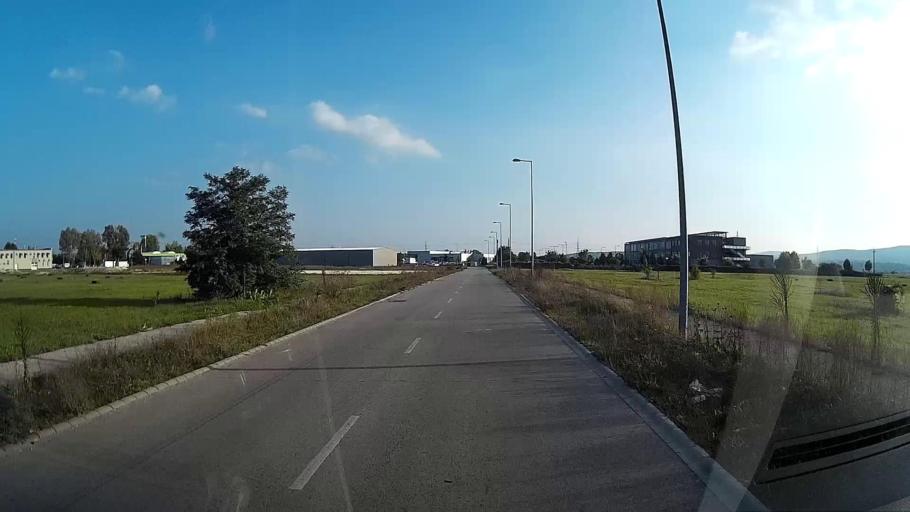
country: HU
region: Pest
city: Szentendre
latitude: 47.6434
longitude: 19.0656
